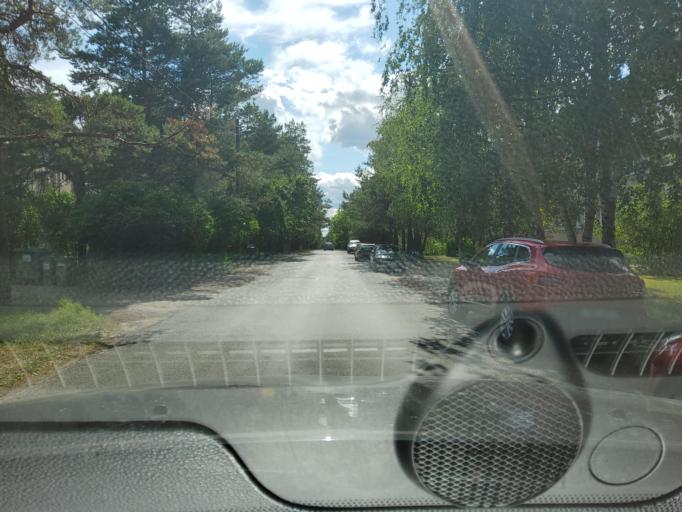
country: EE
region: Harju
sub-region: Saue vald
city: Laagri
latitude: 59.3689
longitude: 24.6470
